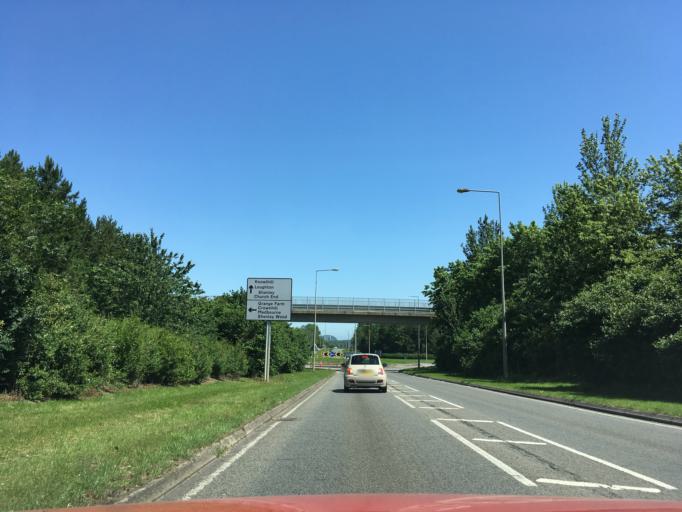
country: GB
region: England
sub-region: Milton Keynes
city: Shenley Church End
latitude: 52.0163
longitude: -0.7863
